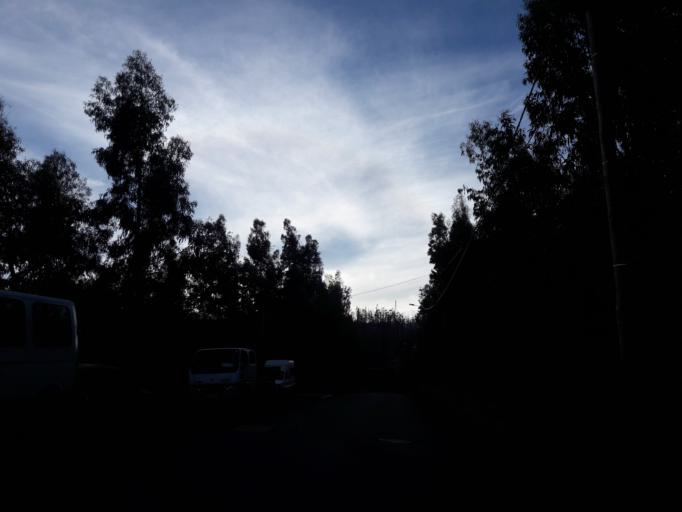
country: PT
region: Madeira
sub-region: Santa Cruz
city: Camacha
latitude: 32.6866
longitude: -16.8586
